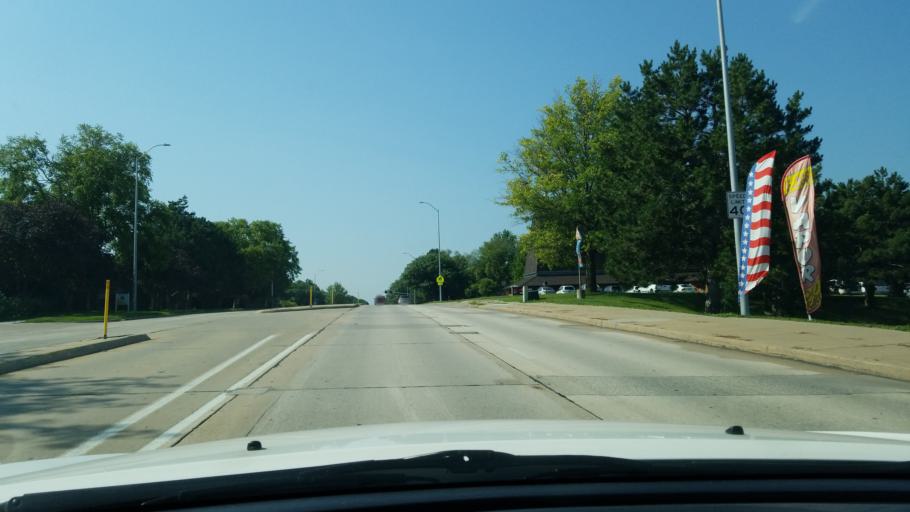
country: US
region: Nebraska
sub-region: Lancaster County
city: Lincoln
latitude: 40.7976
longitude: -96.6251
